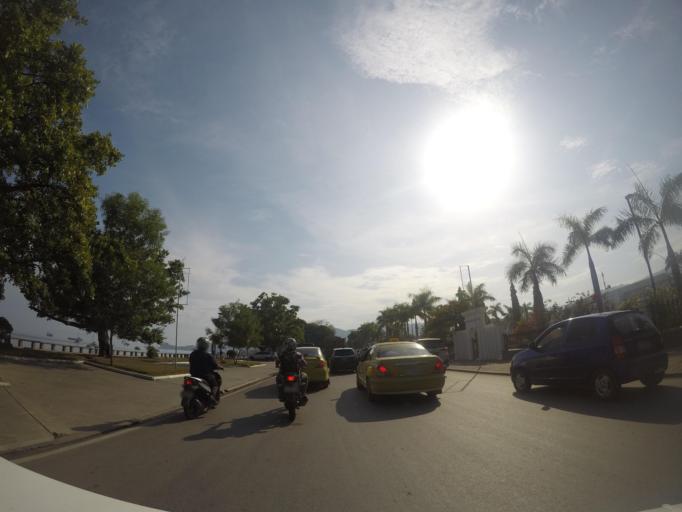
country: TL
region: Dili
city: Dili
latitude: -8.5536
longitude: 125.5776
